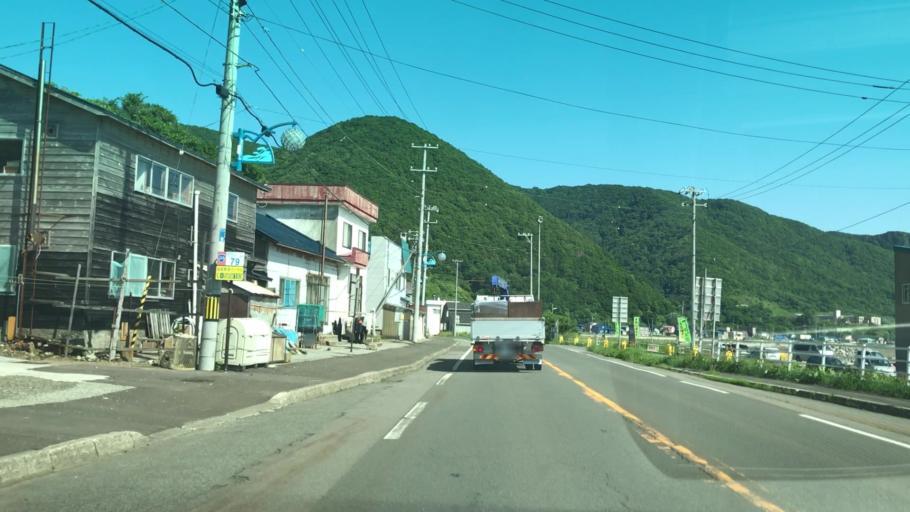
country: JP
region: Hokkaido
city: Iwanai
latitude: 43.1071
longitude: 140.4540
